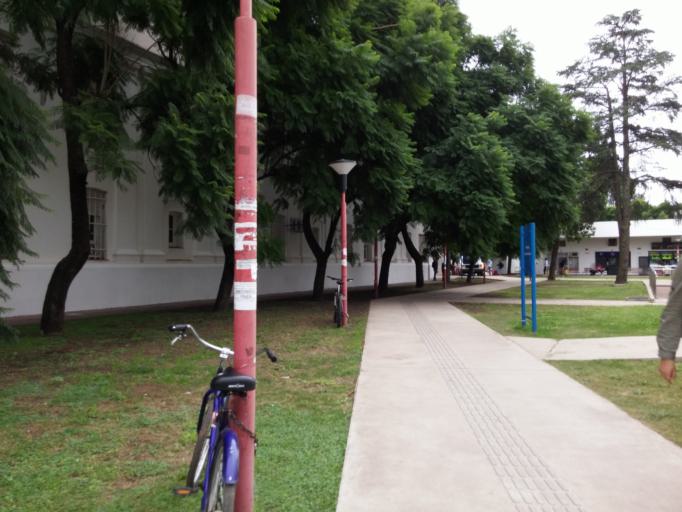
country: AR
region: Cordoba
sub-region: Departamento de Capital
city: Cordoba
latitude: -31.4396
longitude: -64.1882
